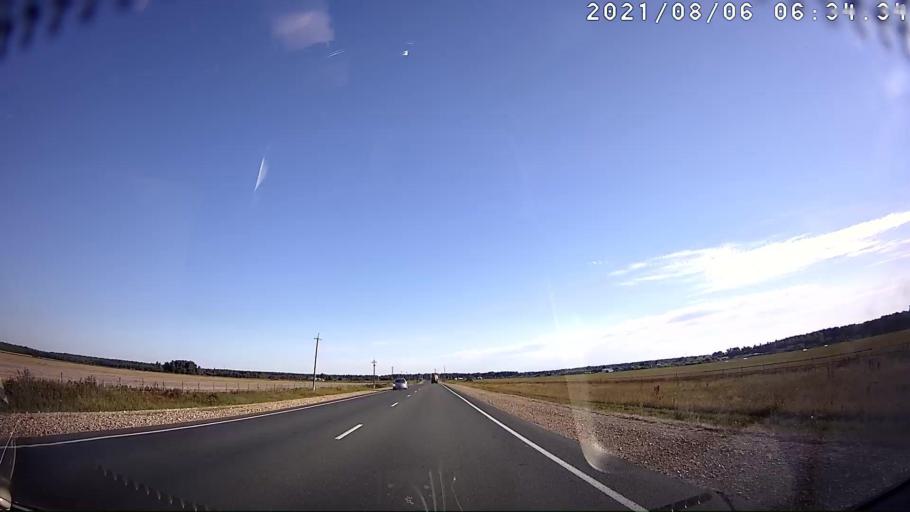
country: RU
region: Mariy-El
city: Krasnogorskiy
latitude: 56.2083
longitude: 48.2363
